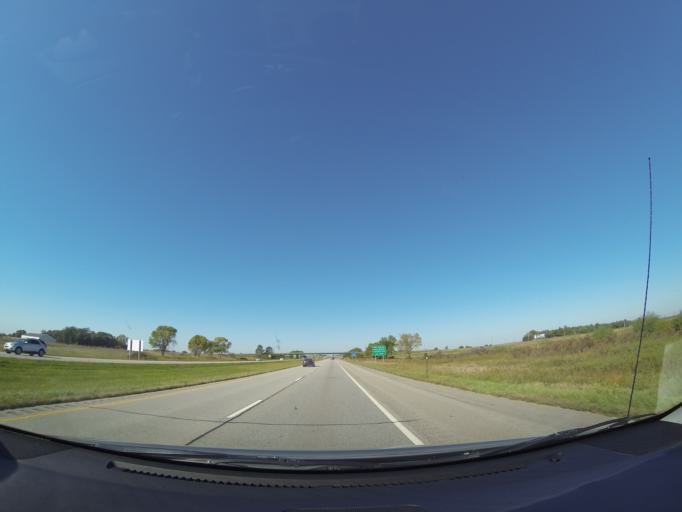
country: US
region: Nebraska
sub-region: Seward County
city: Milford
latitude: 40.8222
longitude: -97.0788
